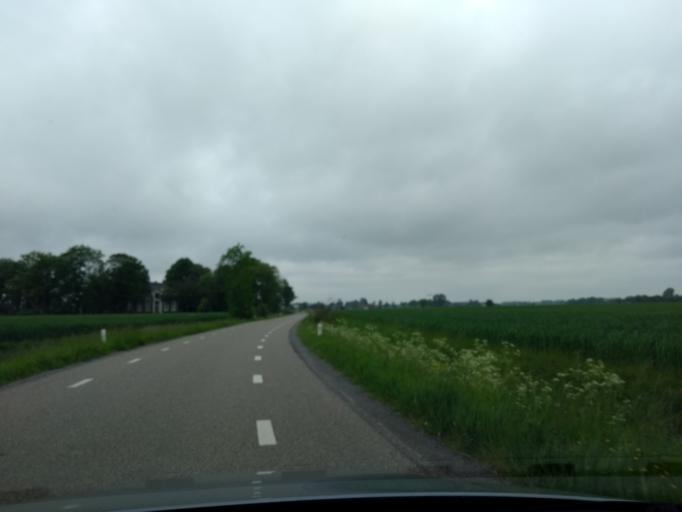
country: NL
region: Groningen
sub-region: Gemeente Zuidhorn
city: Oldehove
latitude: 53.3327
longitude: 6.4269
